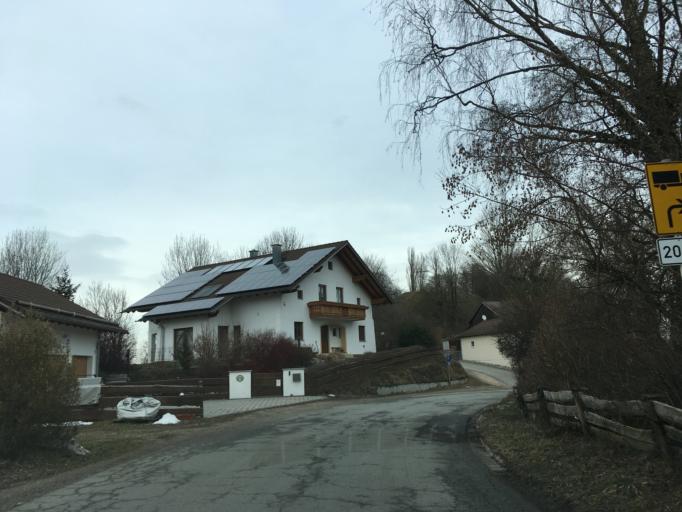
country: DE
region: Bavaria
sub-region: Upper Bavaria
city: Kraiburg am Inn
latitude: 48.1785
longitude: 12.4271
